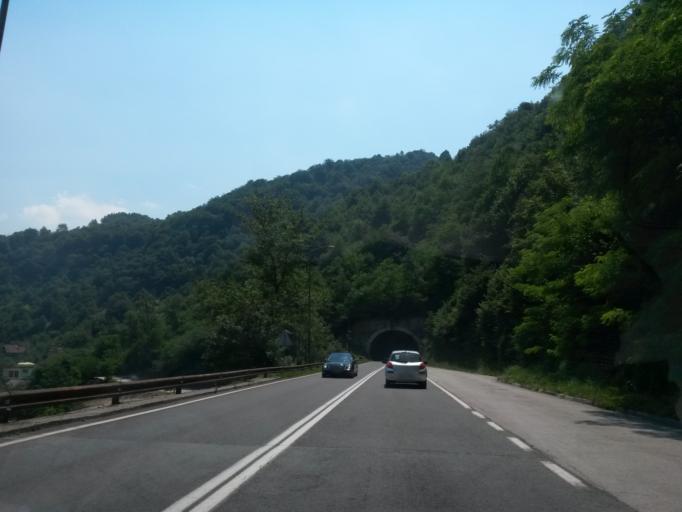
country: BA
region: Federation of Bosnia and Herzegovina
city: Zenica
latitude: 44.3021
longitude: 17.9086
